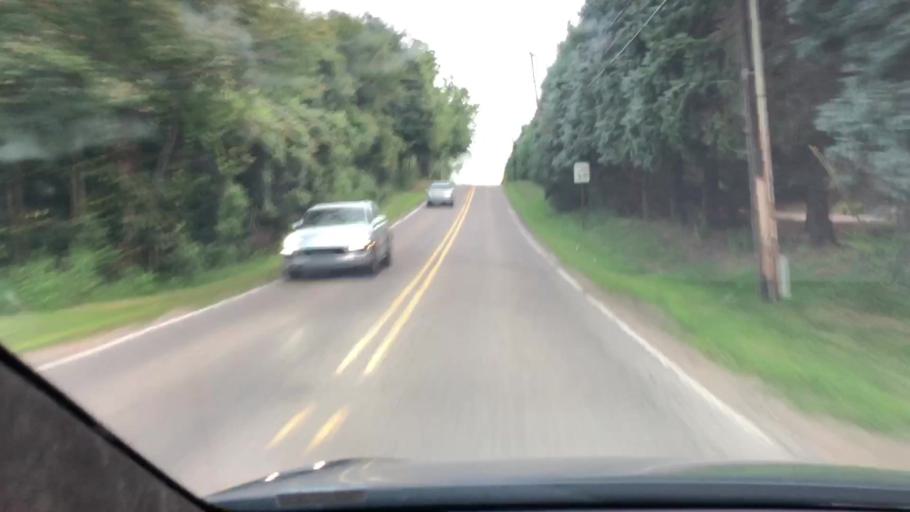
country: US
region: Pennsylvania
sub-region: Butler County
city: Shanor-Northvue
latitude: 40.9022
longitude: -79.9289
